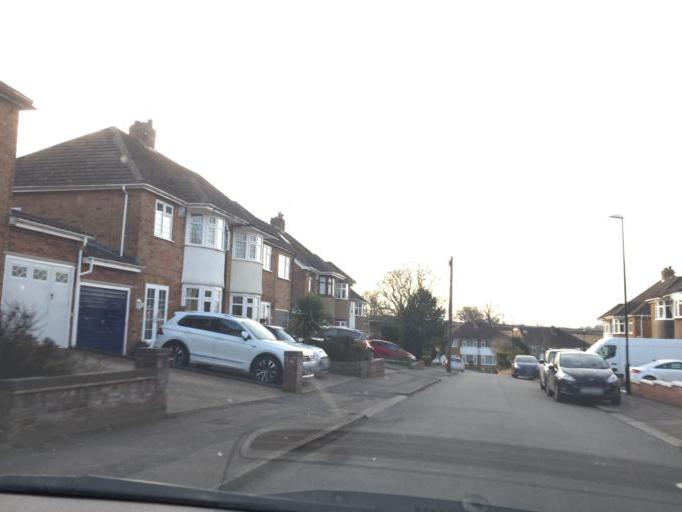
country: GB
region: England
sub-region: Coventry
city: Keresley
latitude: 52.4287
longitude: -1.5698
